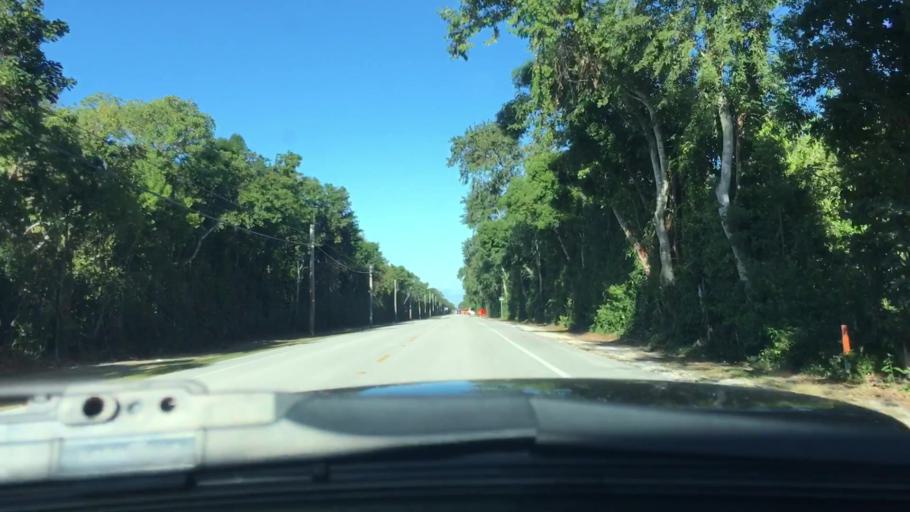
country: US
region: Florida
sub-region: Monroe County
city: North Key Largo
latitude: 25.1831
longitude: -80.3636
